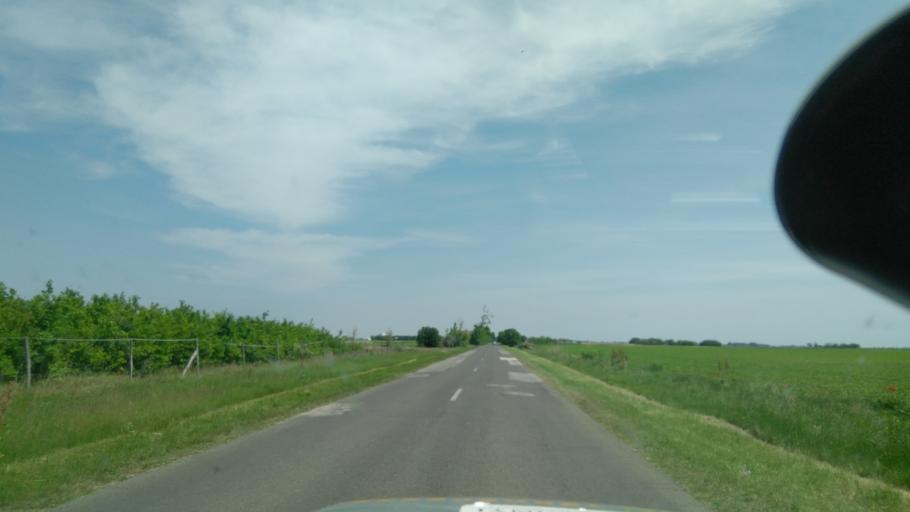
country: HU
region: Csongrad
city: Szekkutas
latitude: 46.5726
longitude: 20.5436
